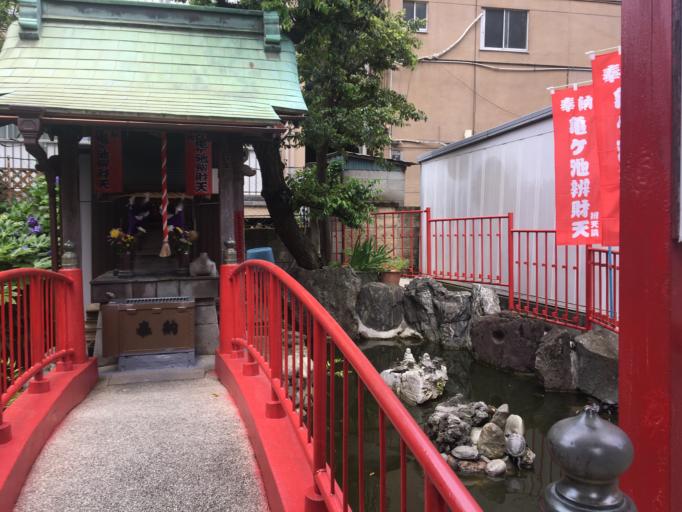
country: JP
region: Saitama
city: Kawaguchi
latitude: 35.7763
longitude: 139.7174
